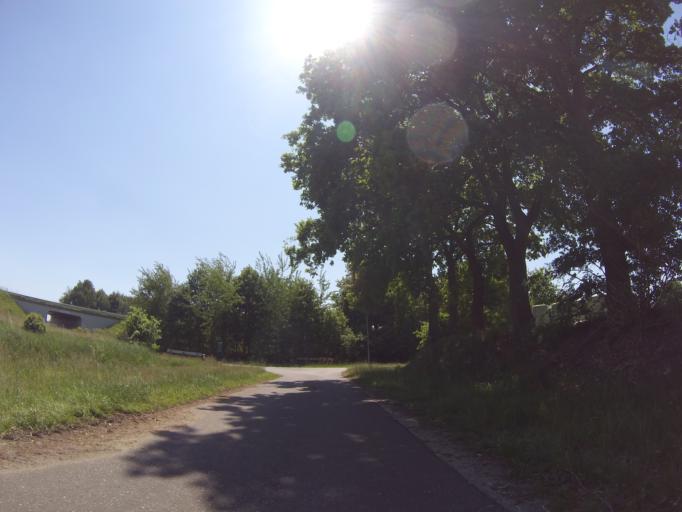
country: NL
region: Drenthe
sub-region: Gemeente Coevorden
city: Sleen
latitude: 52.7560
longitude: 6.8334
